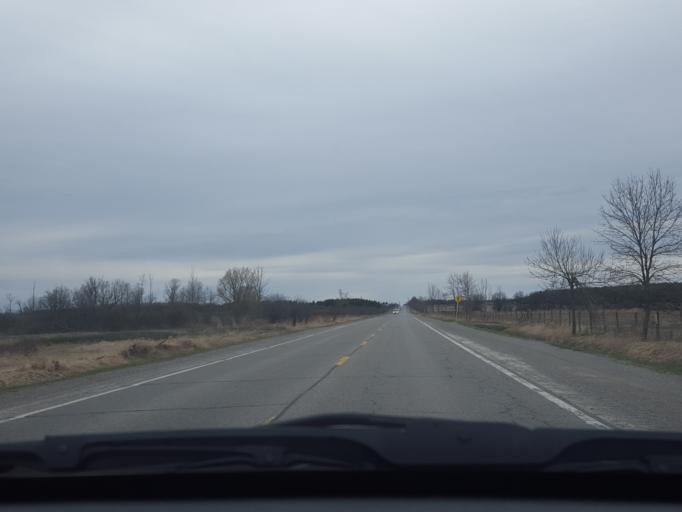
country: CA
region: Ontario
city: Uxbridge
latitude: 44.3041
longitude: -79.1742
